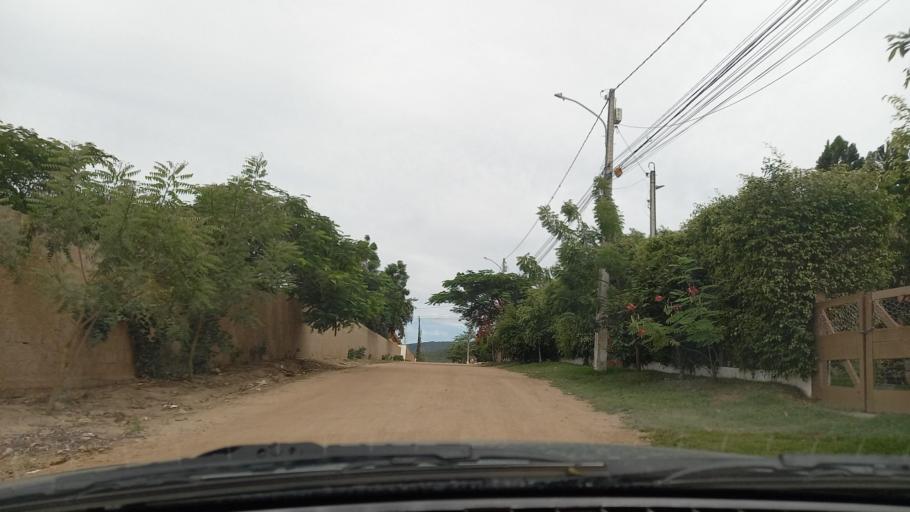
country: BR
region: Pernambuco
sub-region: Gravata
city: Gravata
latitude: -8.1956
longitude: -35.5938
